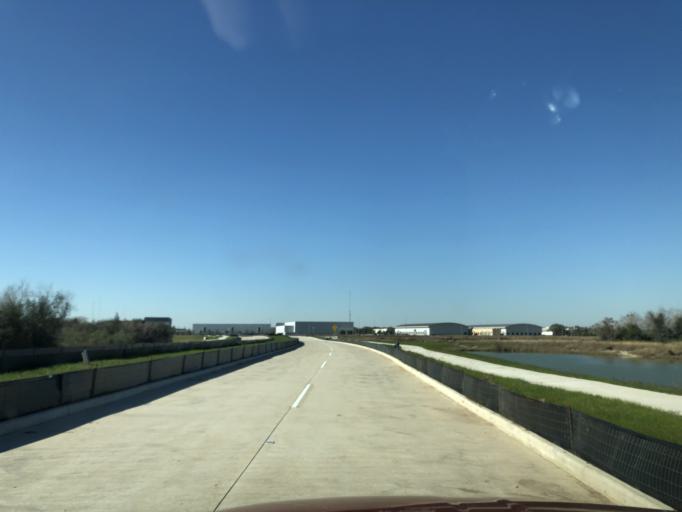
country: US
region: Texas
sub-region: Brazoria County
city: Brookside Village
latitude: 29.5888
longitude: -95.3942
